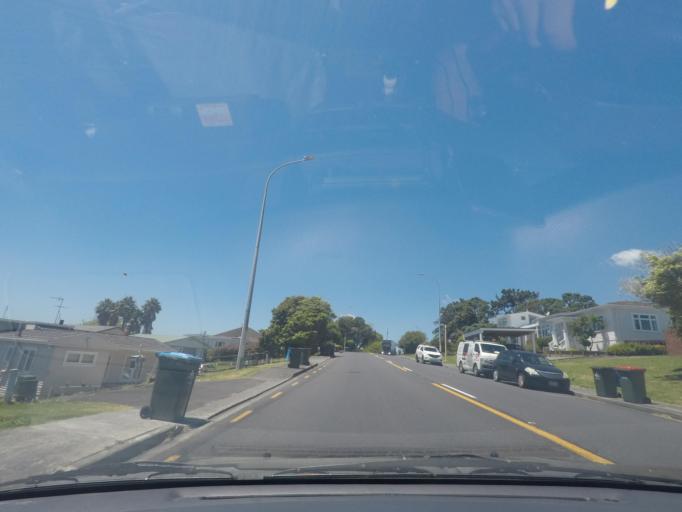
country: NZ
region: Auckland
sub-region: Auckland
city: Auckland
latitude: -36.9303
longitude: 174.7390
